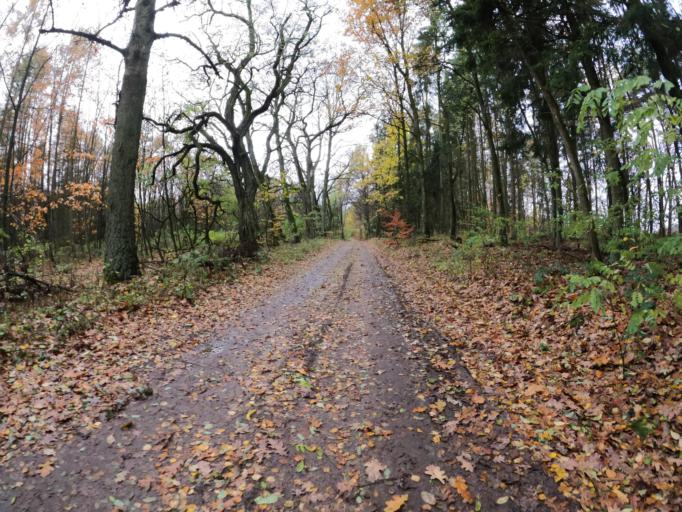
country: PL
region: West Pomeranian Voivodeship
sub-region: Powiat walecki
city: Tuczno
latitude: 53.2663
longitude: 16.2390
